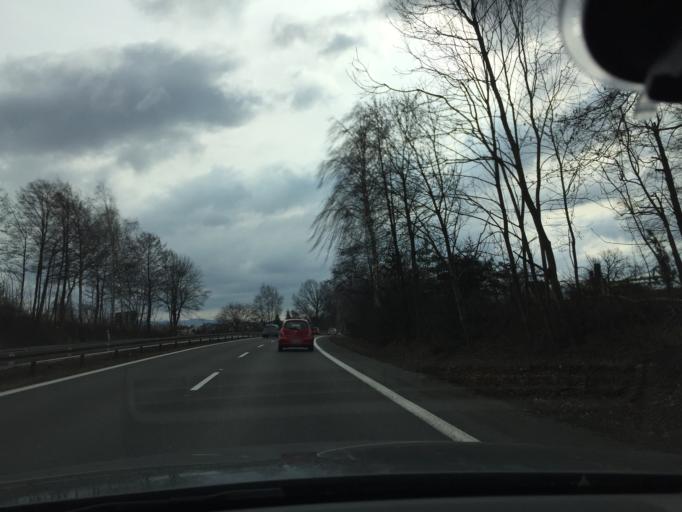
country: PL
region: Silesian Voivodeship
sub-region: Powiat bielski
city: Czechowice-Dziedzice
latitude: 49.9080
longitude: 18.9904
